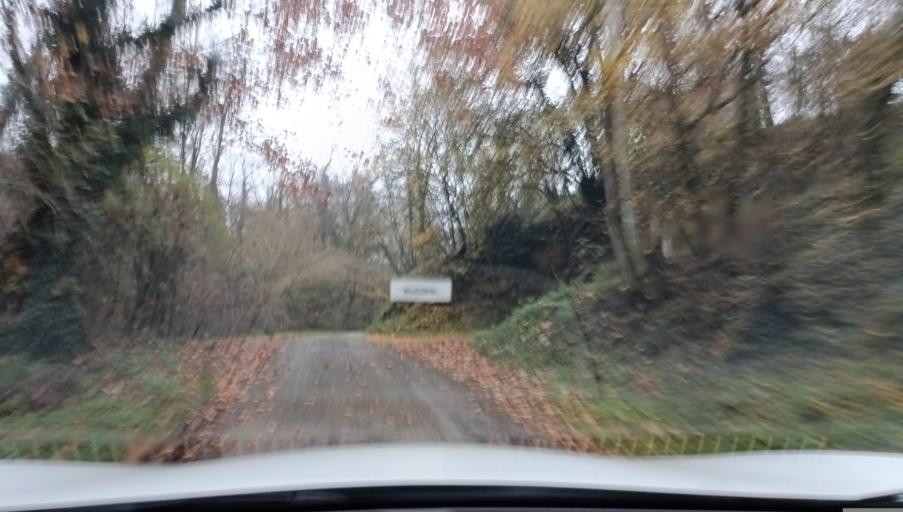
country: FR
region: Rhone-Alpes
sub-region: Departement de l'Isere
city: Chuzelles
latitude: 45.5680
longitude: 4.8719
